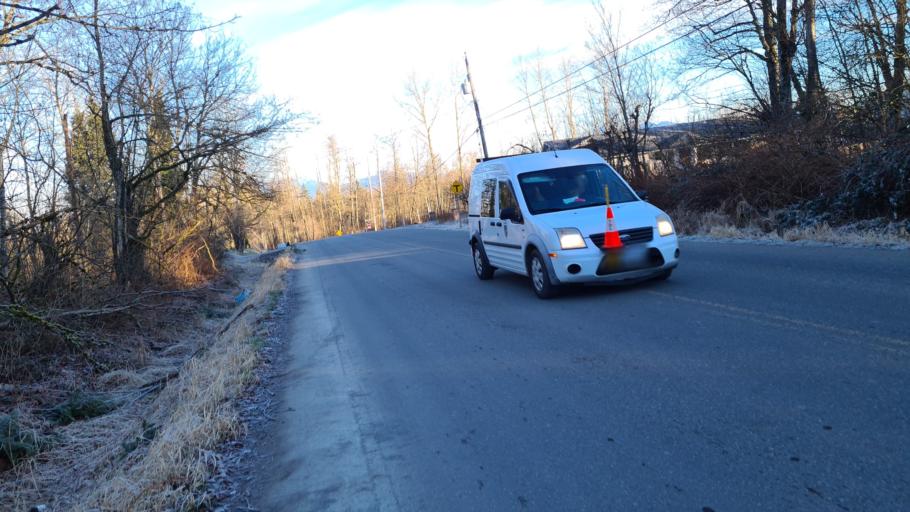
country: CA
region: British Columbia
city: Walnut Grove
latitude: 49.1398
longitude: -122.6723
